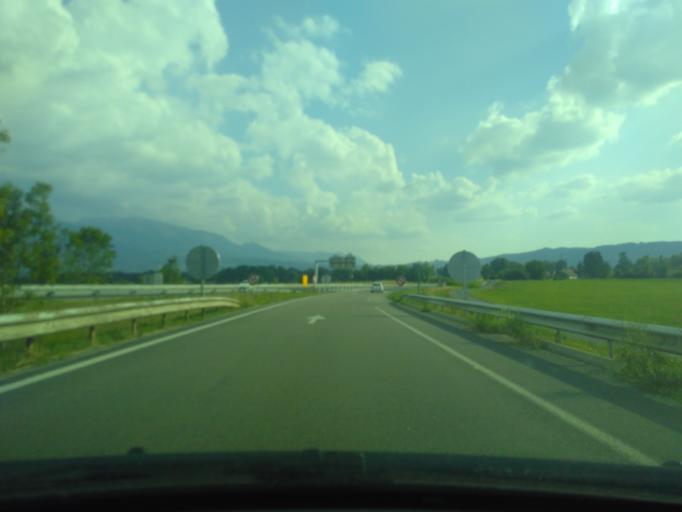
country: FR
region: Rhone-Alpes
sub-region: Departement de la Haute-Savoie
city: Arenthon
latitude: 46.1179
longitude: 6.3254
